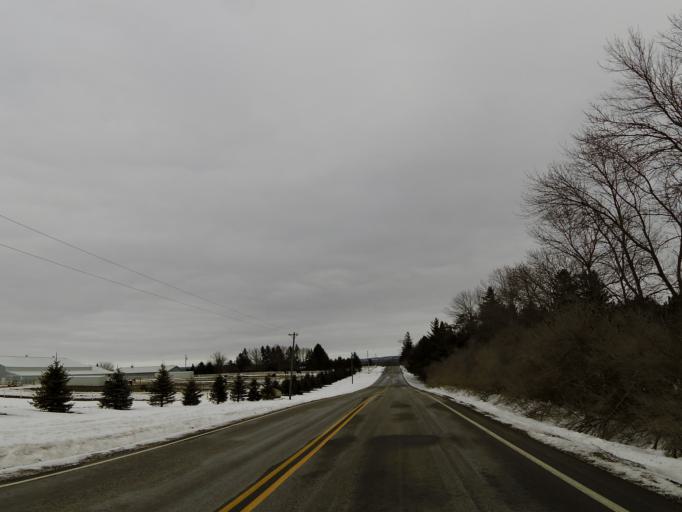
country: US
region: Wisconsin
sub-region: Pierce County
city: Prescott
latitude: 44.8190
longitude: -92.8102
